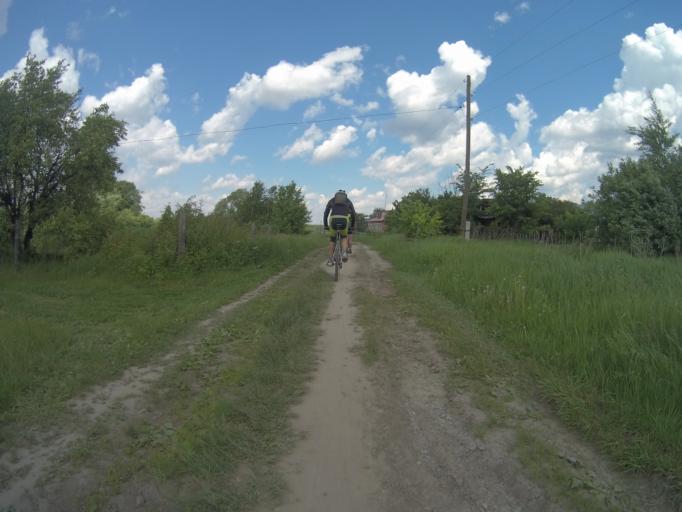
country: RU
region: Vladimir
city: Raduzhnyy
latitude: 56.0056
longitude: 40.2205
